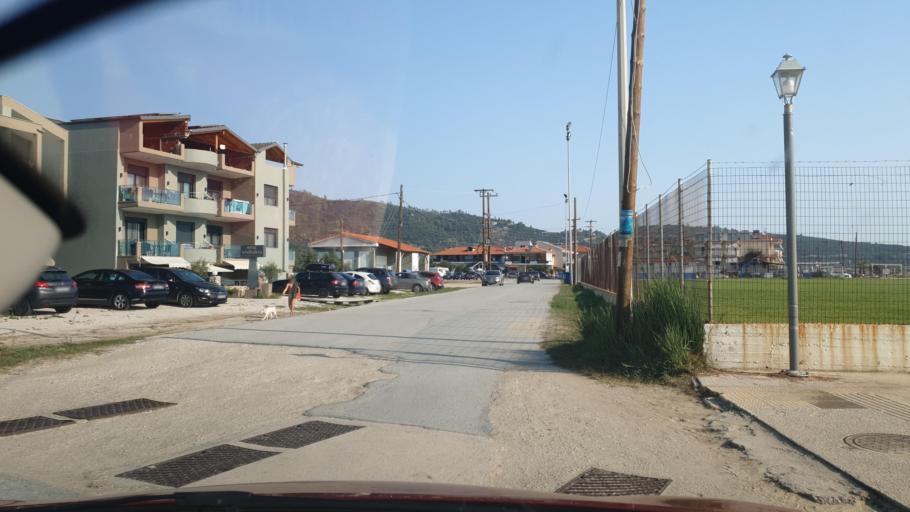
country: GR
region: Central Macedonia
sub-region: Nomos Chalkidikis
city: Sarti
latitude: 40.0872
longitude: 23.9782
